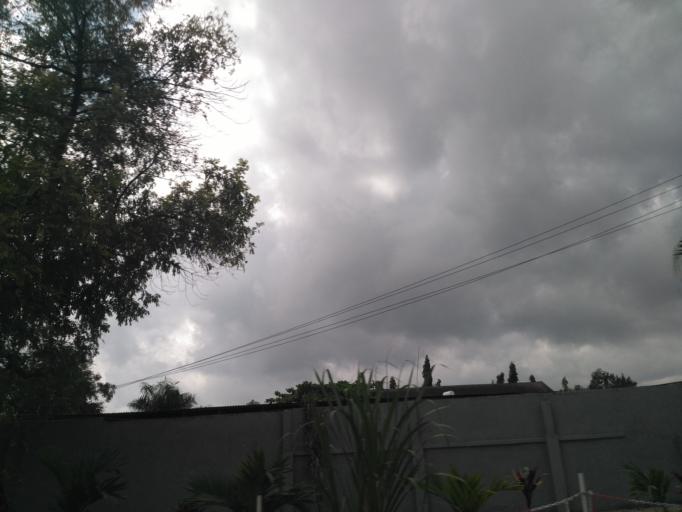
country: TZ
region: Dar es Salaam
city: Magomeni
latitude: -6.7578
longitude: 39.2464
